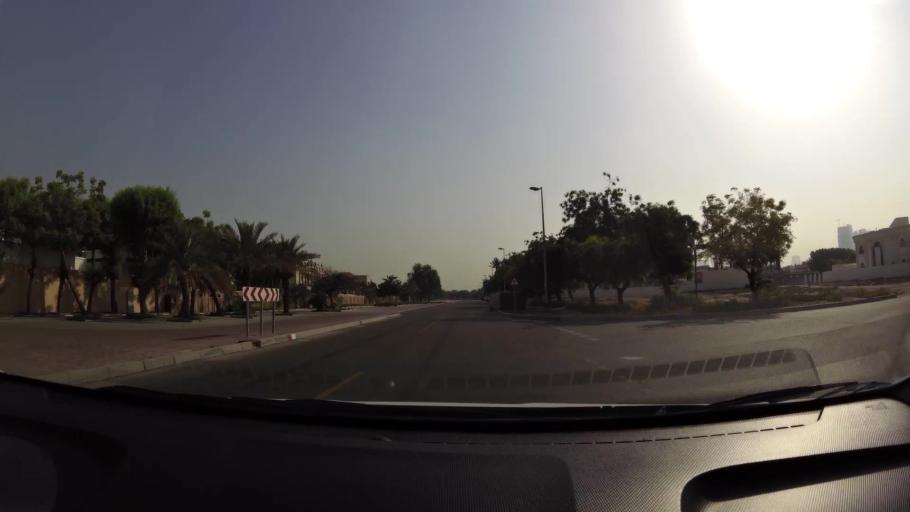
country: AE
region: Ash Shariqah
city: Sharjah
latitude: 25.3130
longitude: 55.3438
